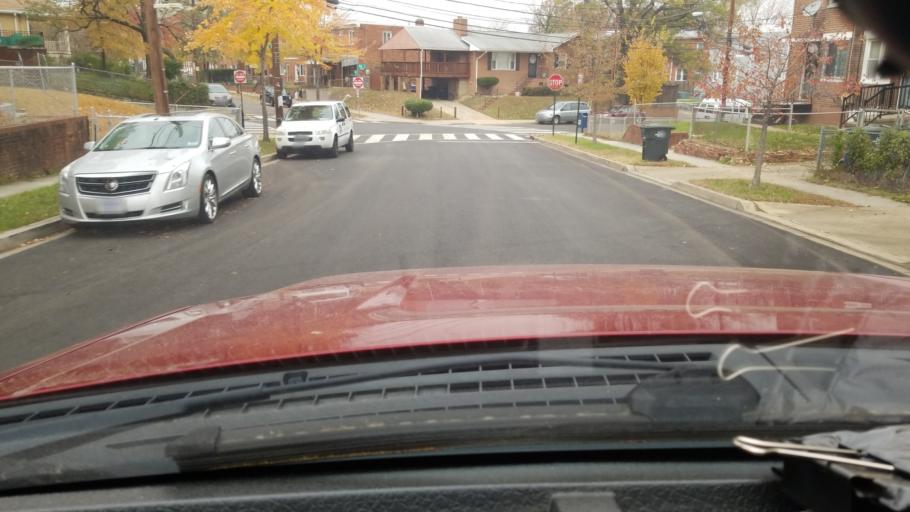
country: US
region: Maryland
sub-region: Prince George's County
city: Capitol Heights
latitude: 38.8855
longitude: -76.9232
